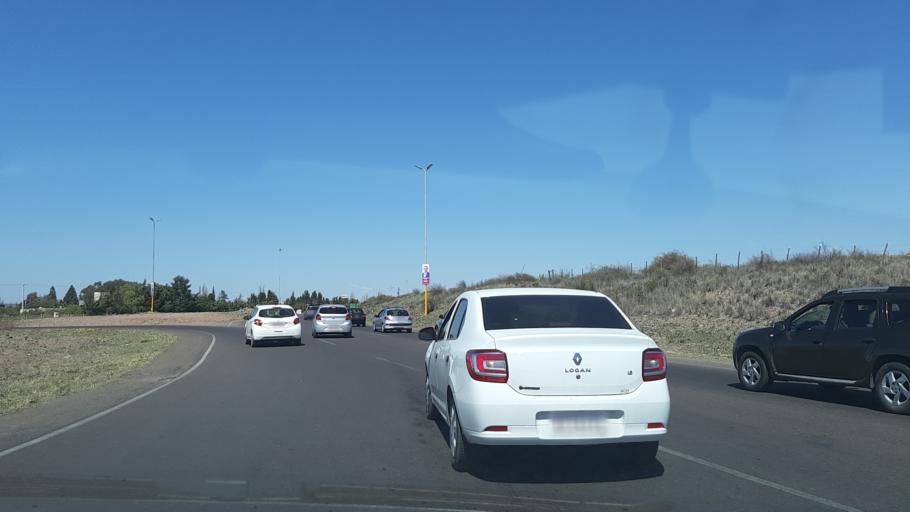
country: AR
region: Mendoza
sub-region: Departamento de Godoy Cruz
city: Godoy Cruz
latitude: -32.9703
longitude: -68.8815
